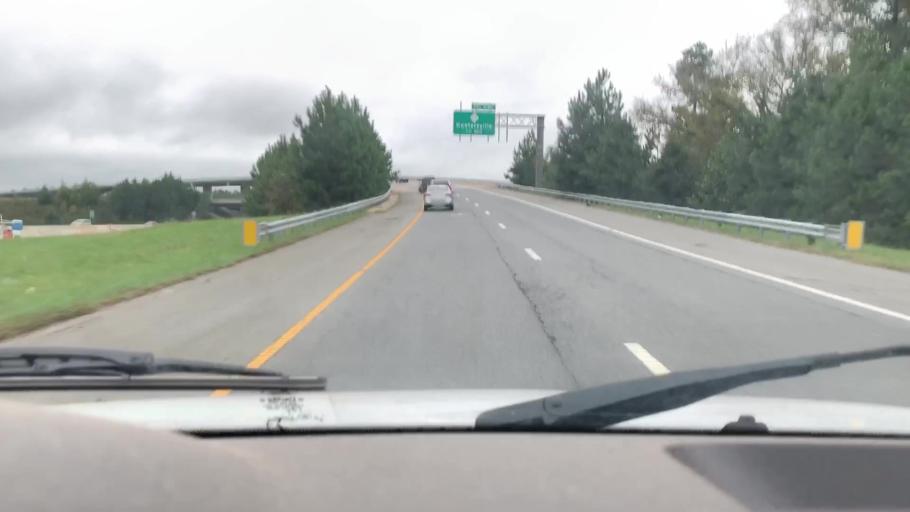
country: US
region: North Carolina
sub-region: Mecklenburg County
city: Huntersville
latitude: 35.3662
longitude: -80.8432
